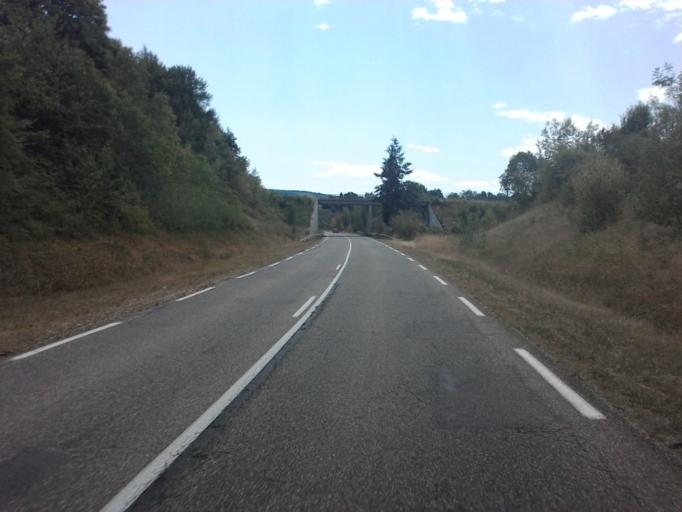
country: FR
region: Franche-Comte
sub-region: Departement du Jura
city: Saint-Amour
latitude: 46.4429
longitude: 5.3483
